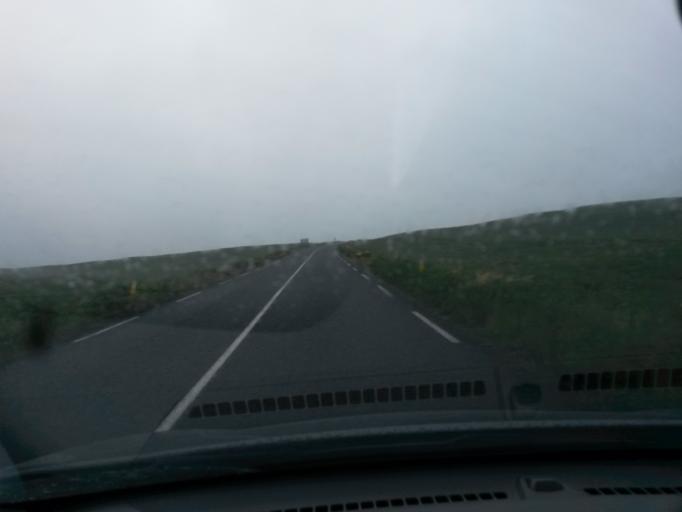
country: IS
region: South
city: Vestmannaeyjar
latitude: 63.5000
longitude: -19.4072
